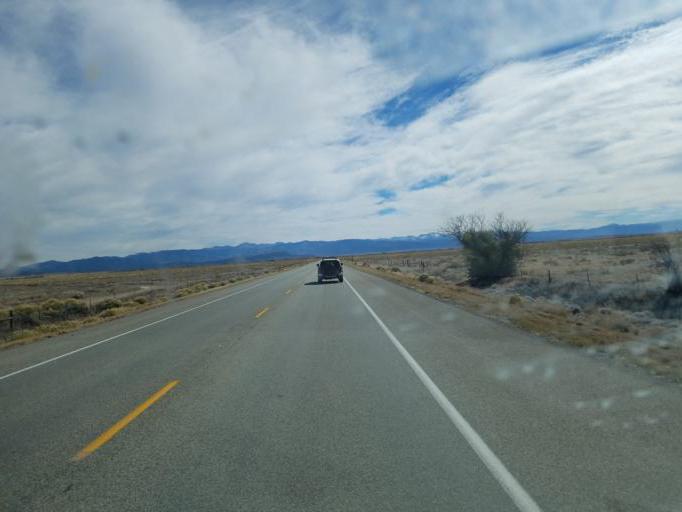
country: US
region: Colorado
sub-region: Alamosa County
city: Alamosa East
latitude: 37.4576
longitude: -105.5551
